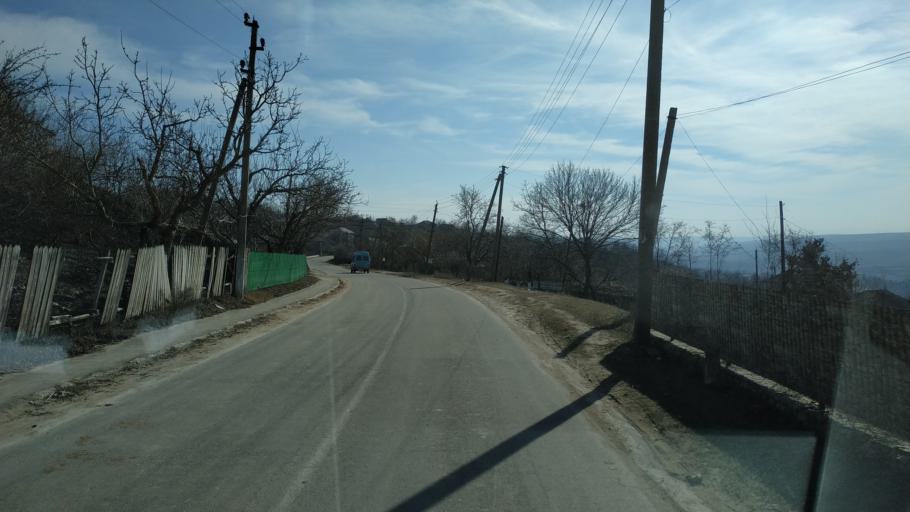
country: MD
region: Nisporeni
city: Nisporeni
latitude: 47.2245
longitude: 28.0456
